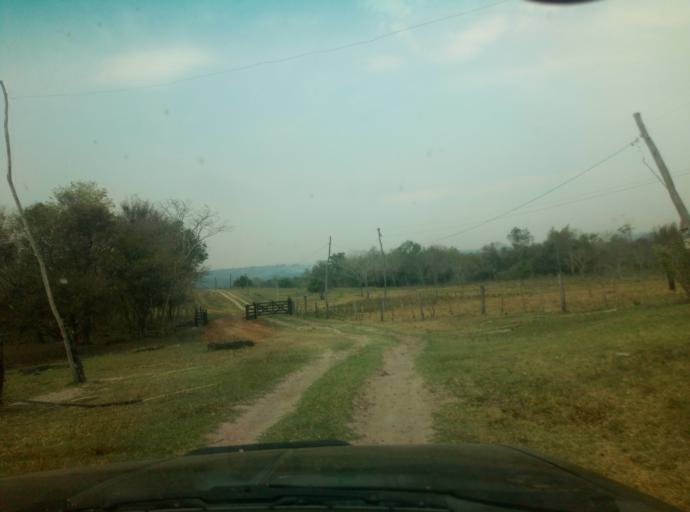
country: PY
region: Caaguazu
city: San Joaquin
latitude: -25.1042
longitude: -56.1271
